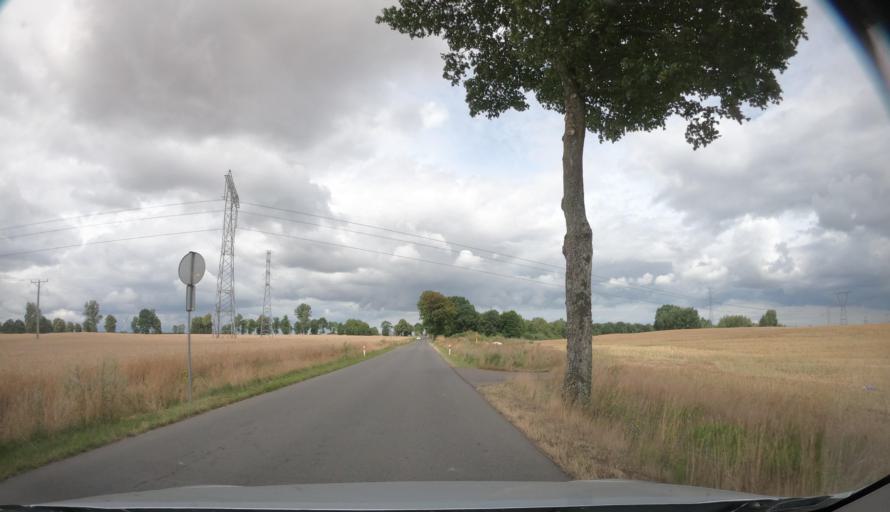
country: PL
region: West Pomeranian Voivodeship
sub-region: Koszalin
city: Koszalin
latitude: 54.1517
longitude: 16.0822
